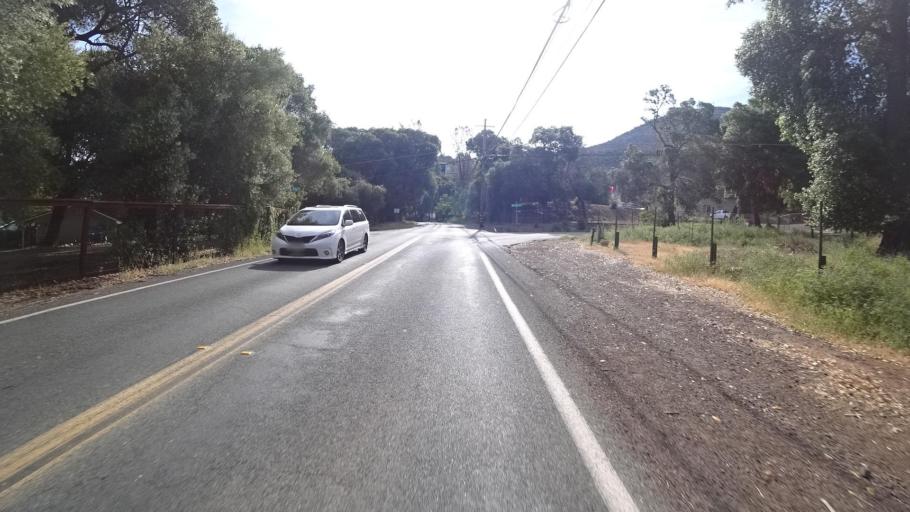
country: US
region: California
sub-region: Lake County
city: Soda Bay
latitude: 39.0012
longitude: -122.7894
